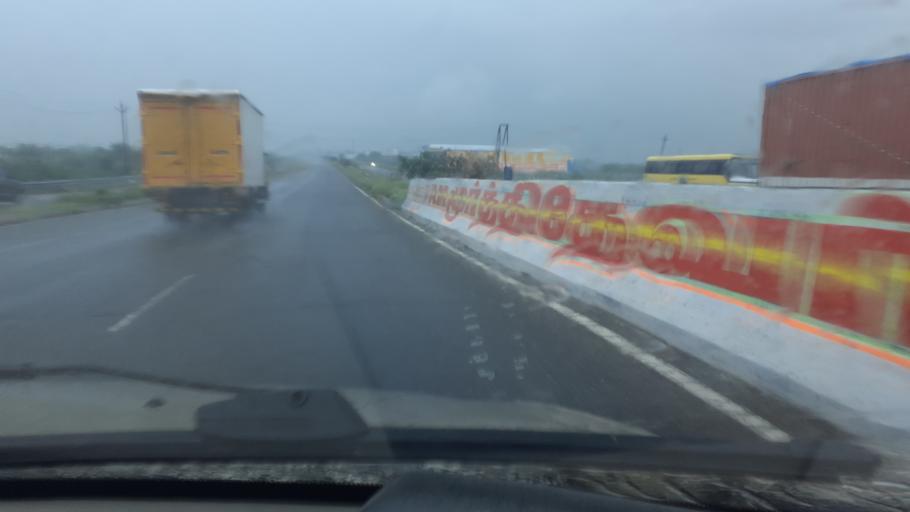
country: IN
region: Tamil Nadu
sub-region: Virudhunagar
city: Virudunagar
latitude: 9.5817
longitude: 77.9433
